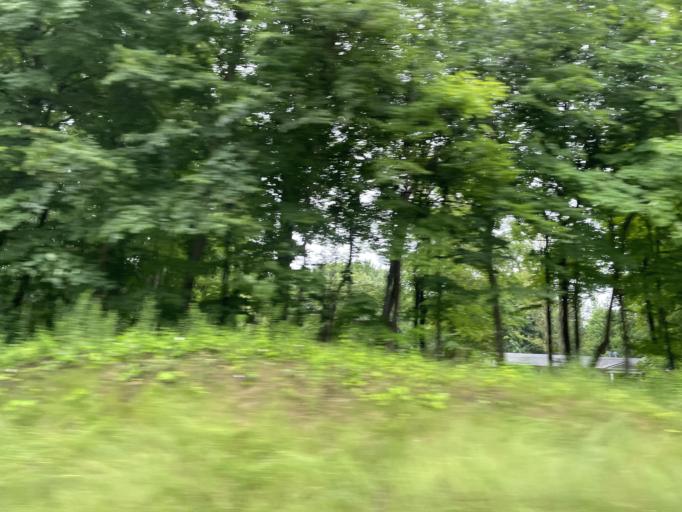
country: CA
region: Ontario
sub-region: Wellington County
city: Guelph
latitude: 43.4456
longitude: -80.2498
